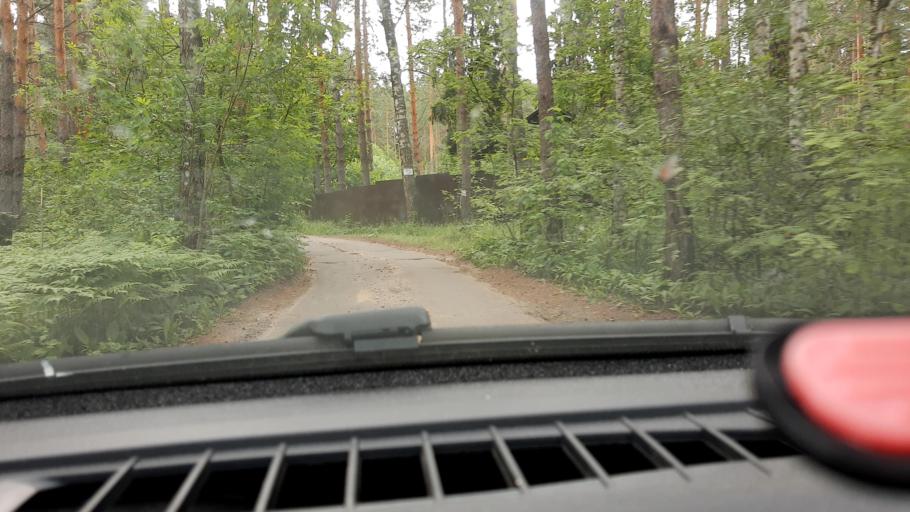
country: RU
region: Nizjnij Novgorod
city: Afonino
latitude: 56.1861
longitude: 44.1096
